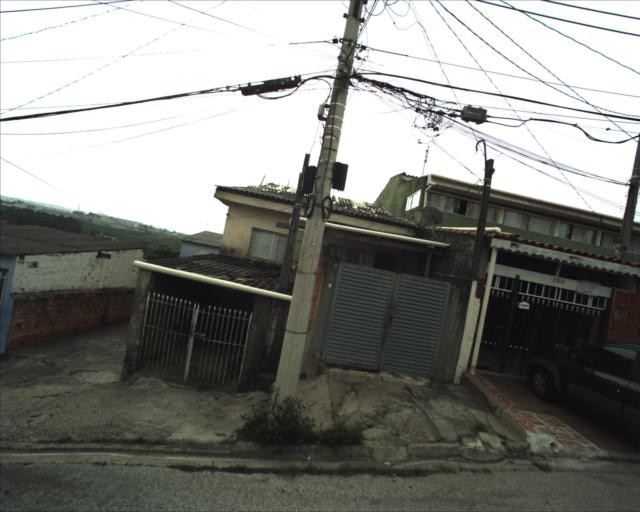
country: BR
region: Sao Paulo
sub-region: Sorocaba
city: Sorocaba
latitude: -23.4610
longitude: -47.4402
